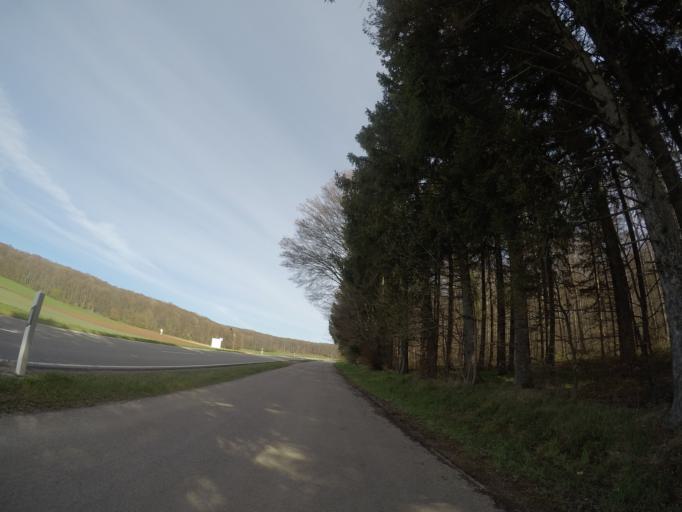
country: DE
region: Baden-Wuerttemberg
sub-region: Regierungsbezirk Stuttgart
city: Hohenstadt
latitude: 48.5281
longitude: 9.6546
